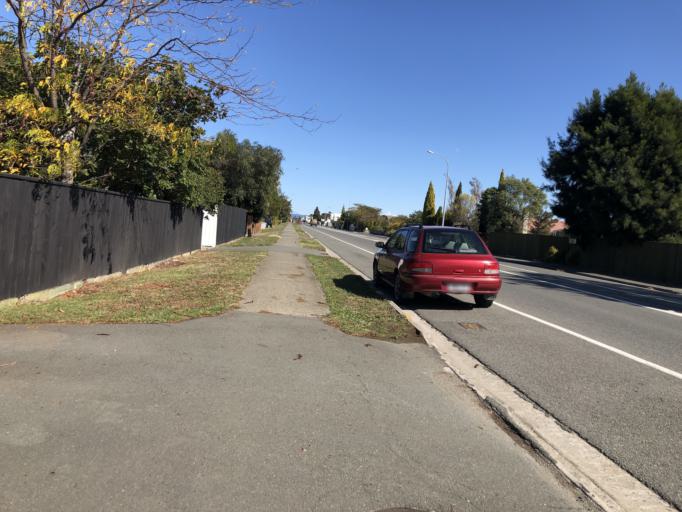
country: NZ
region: Tasman
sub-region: Tasman District
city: Richmond
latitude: -41.3397
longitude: 173.1770
